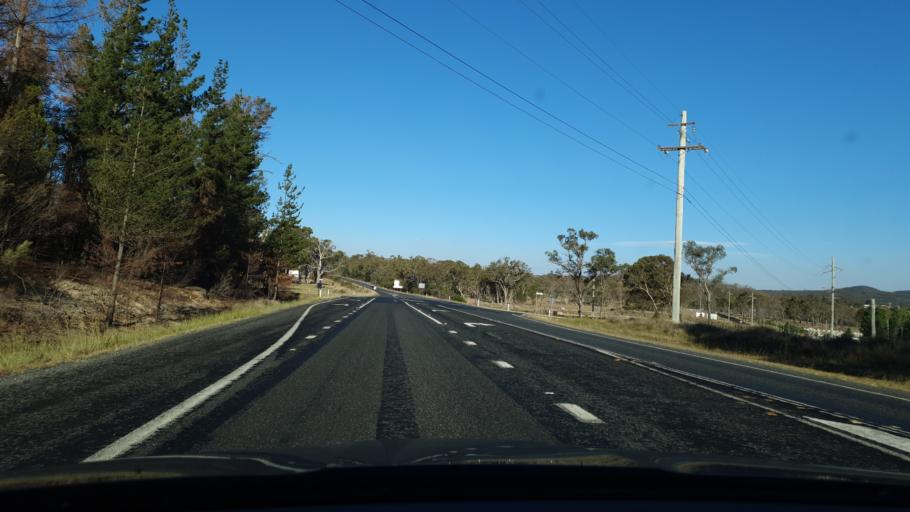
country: AU
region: Queensland
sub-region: Southern Downs
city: Stanthorpe
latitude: -28.6438
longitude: 151.9312
